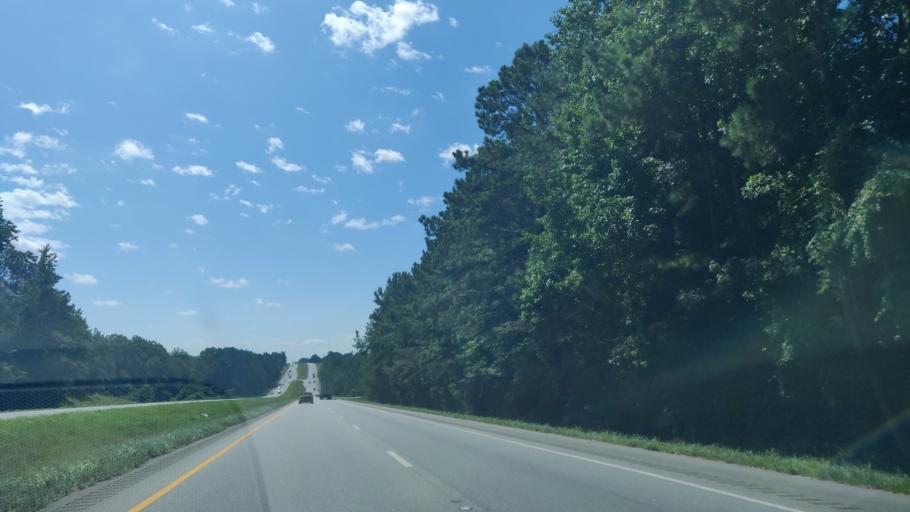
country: US
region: Alabama
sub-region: Lee County
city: Smiths Station
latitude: 32.5547
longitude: -85.1129
